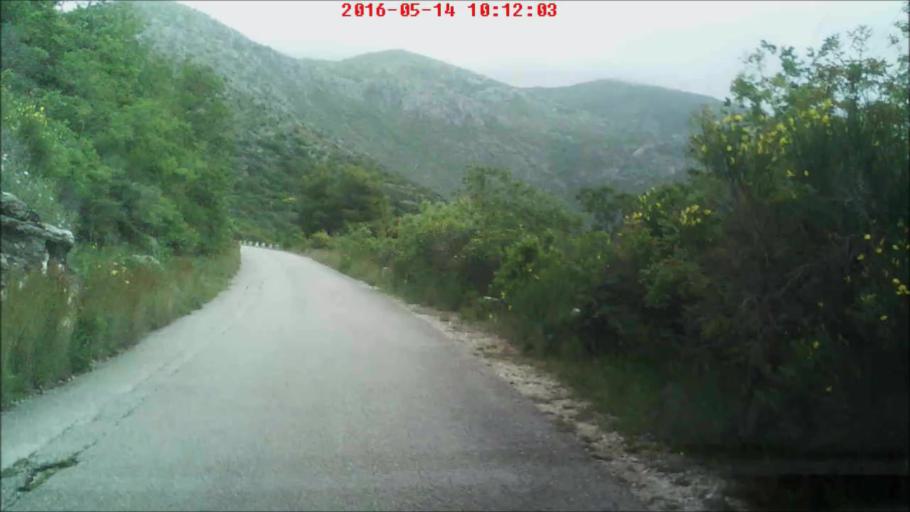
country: HR
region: Dubrovacko-Neretvanska
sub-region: Grad Dubrovnik
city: Mokosica
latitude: 42.7352
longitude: 17.9461
